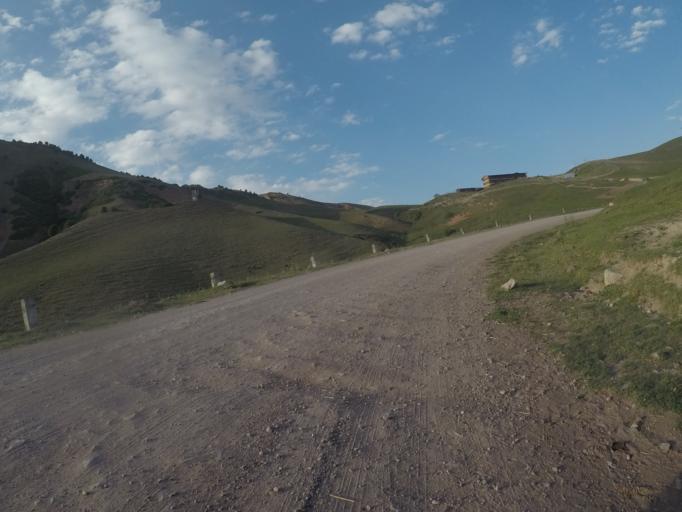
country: KG
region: Chuy
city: Bishkek
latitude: 42.6417
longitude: 74.6248
